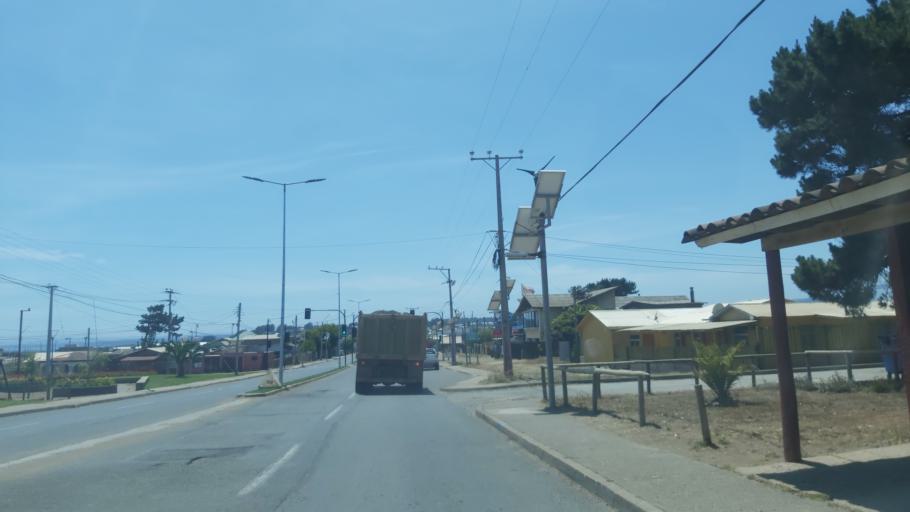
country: CL
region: Maule
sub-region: Provincia de Cauquenes
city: Cauquenes
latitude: -35.8118
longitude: -72.5724
